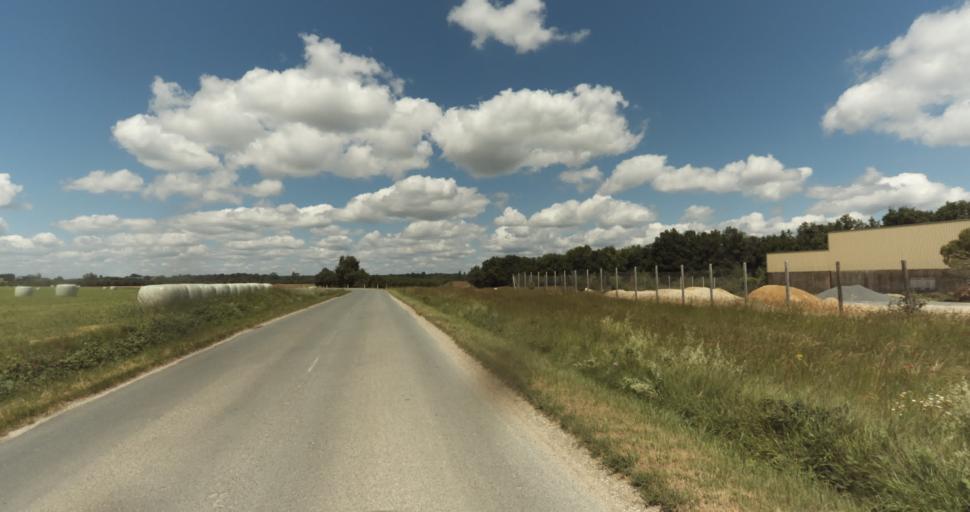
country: FR
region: Aquitaine
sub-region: Departement de la Dordogne
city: Beaumont-du-Perigord
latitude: 44.7123
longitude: 0.8091
